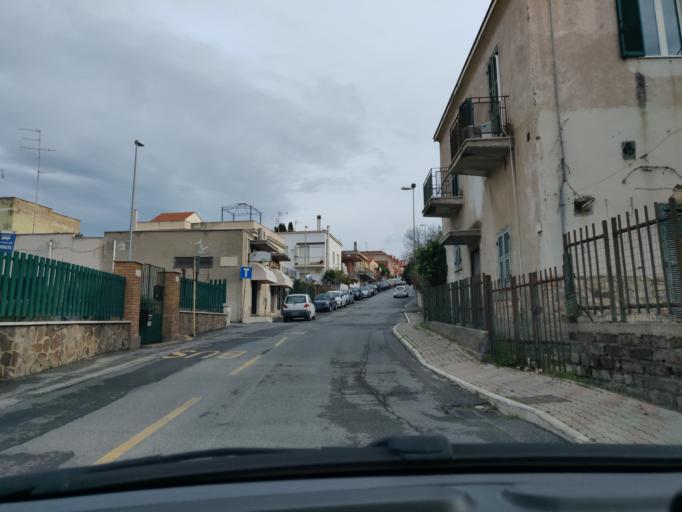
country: IT
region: Latium
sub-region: Citta metropolitana di Roma Capitale
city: Civitavecchia
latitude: 42.0956
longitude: 11.8086
